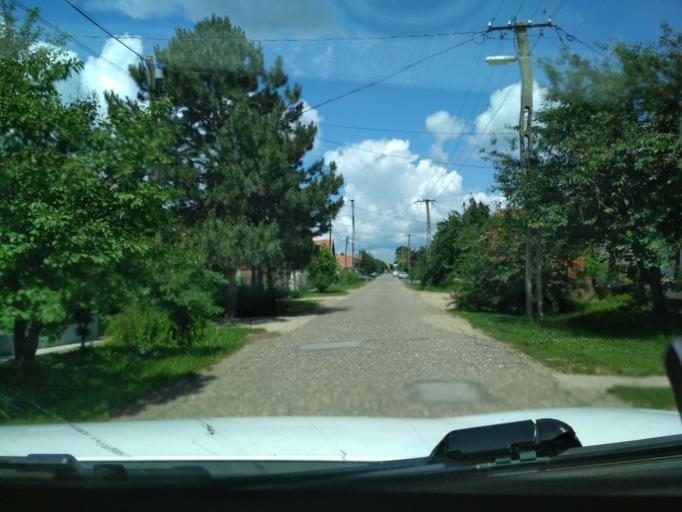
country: HU
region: Jasz-Nagykun-Szolnok
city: Tiszafured
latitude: 47.6094
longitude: 20.7741
